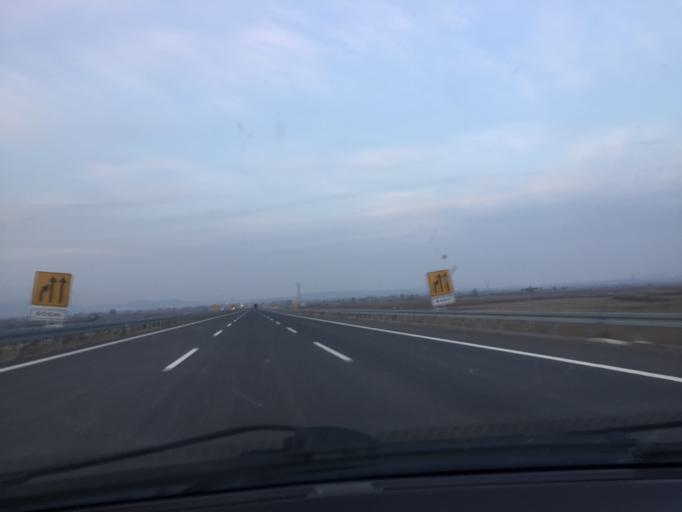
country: TR
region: Manisa
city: Halitpasa
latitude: 38.7113
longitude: 27.6476
